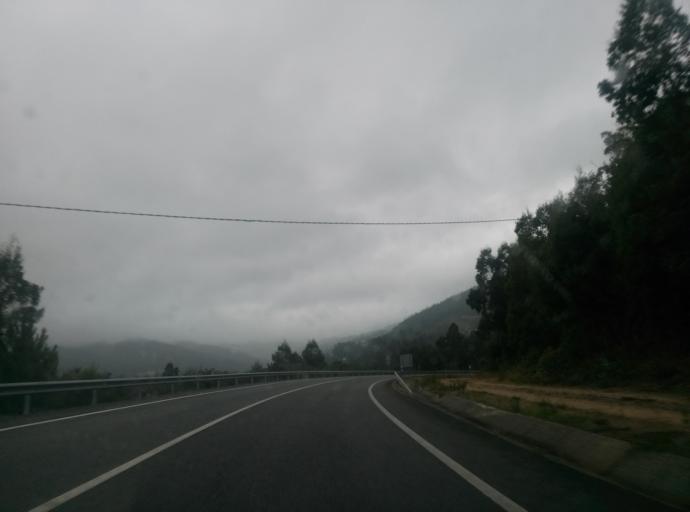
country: ES
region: Galicia
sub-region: Provincia de Lugo
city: Viveiro
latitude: 43.5741
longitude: -7.6338
